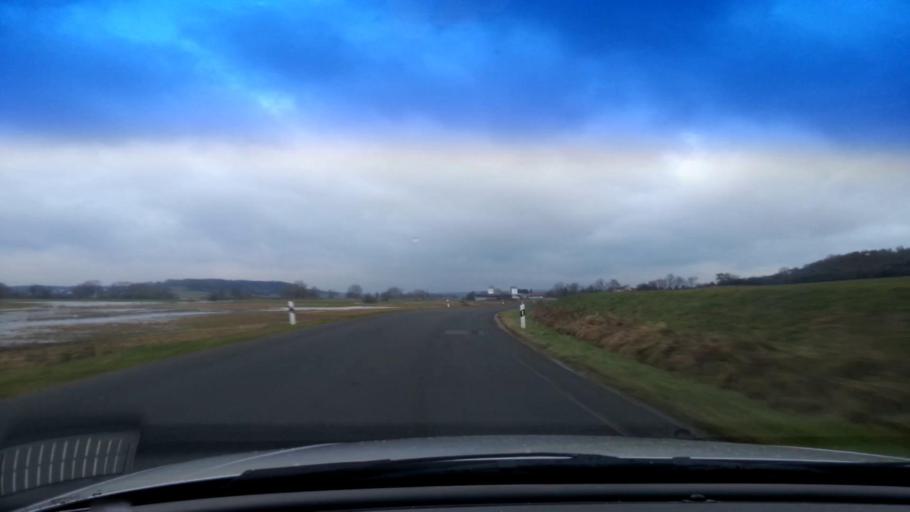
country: DE
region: Bavaria
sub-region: Upper Franconia
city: Burgebrach
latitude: 49.8324
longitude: 10.7740
